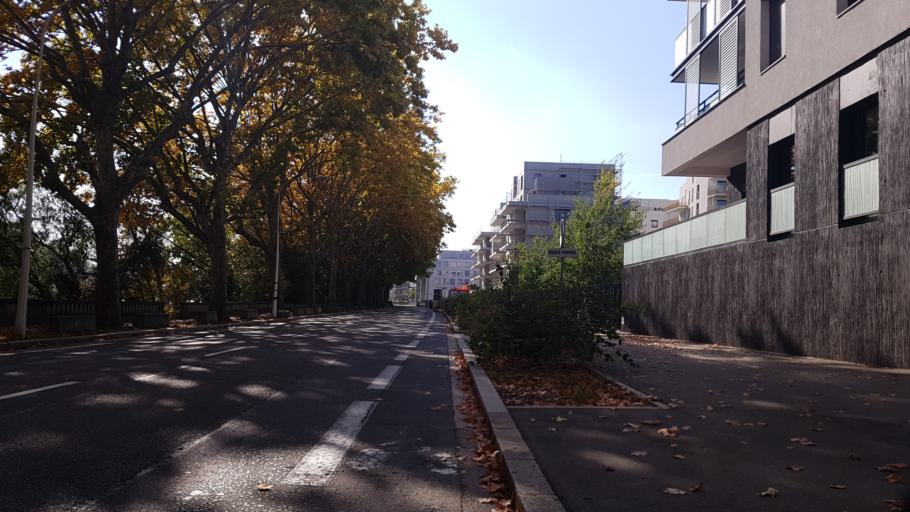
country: FR
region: Rhone-Alpes
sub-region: Departement du Rhone
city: Caluire-et-Cuire
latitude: 45.7902
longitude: 4.8174
